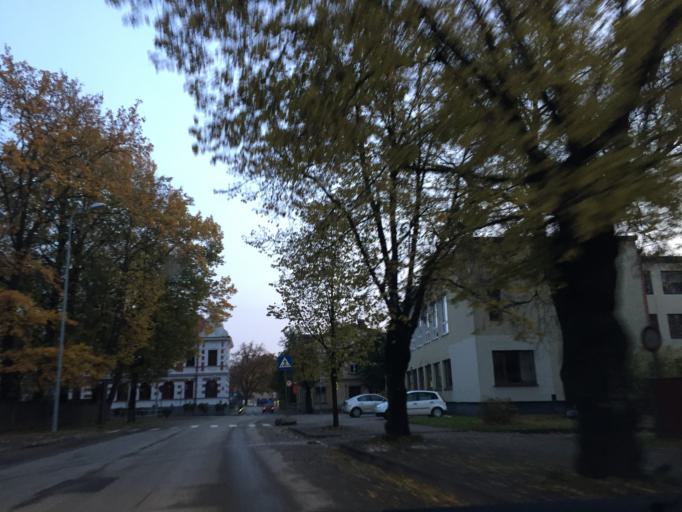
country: LV
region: Cesu Rajons
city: Cesis
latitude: 57.3140
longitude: 25.2796
